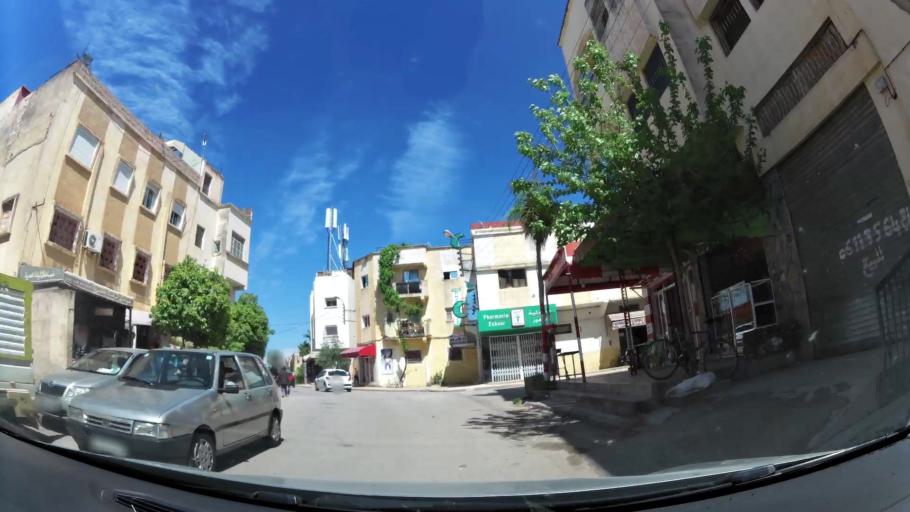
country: MA
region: Fes-Boulemane
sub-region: Fes
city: Fes
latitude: 34.0045
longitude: -4.9831
